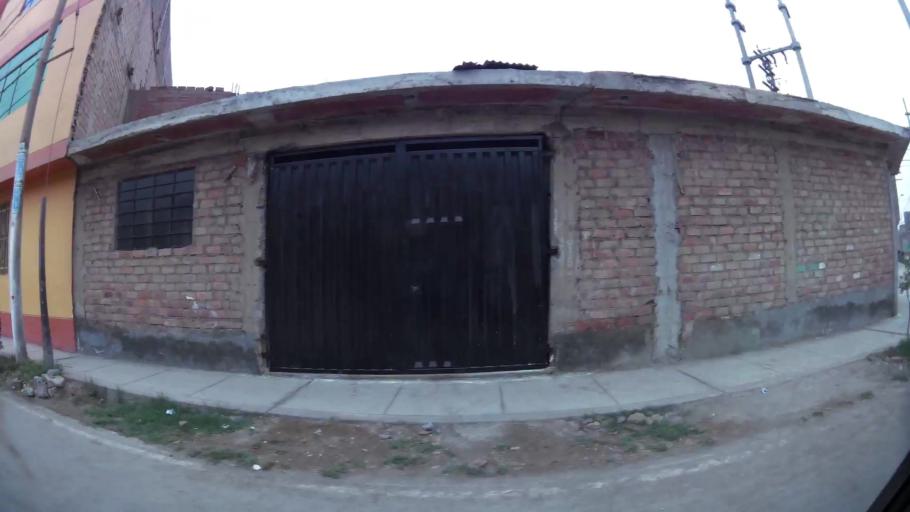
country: PE
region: Lima
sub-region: Lima
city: Urb. Santo Domingo
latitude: -11.8859
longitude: -77.0673
